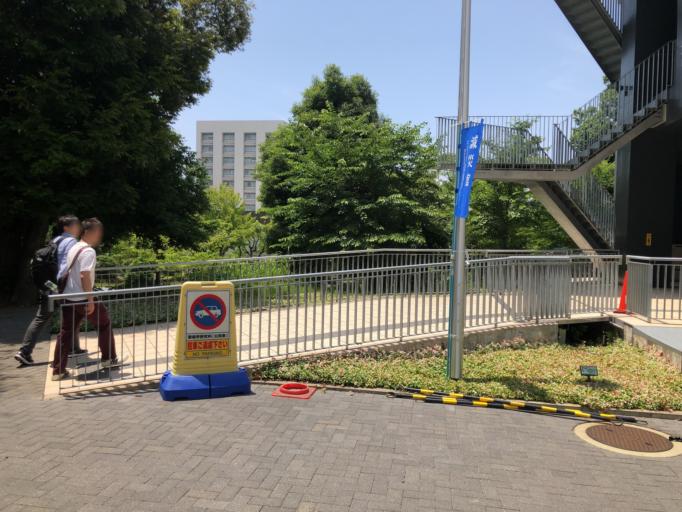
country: JP
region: Aichi
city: Nagoya-shi
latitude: 35.1561
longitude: 136.9668
